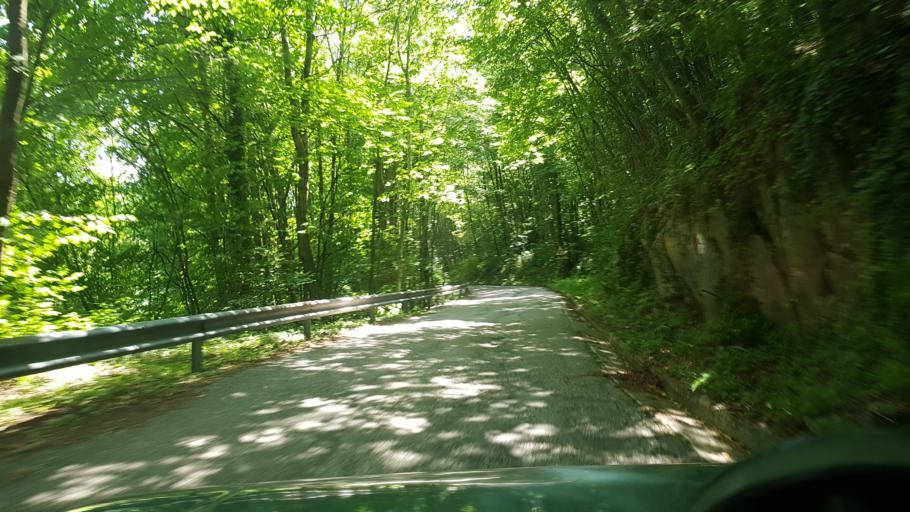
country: IT
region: Friuli Venezia Giulia
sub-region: Provincia di Udine
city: Lusevera
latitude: 46.2518
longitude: 13.2801
